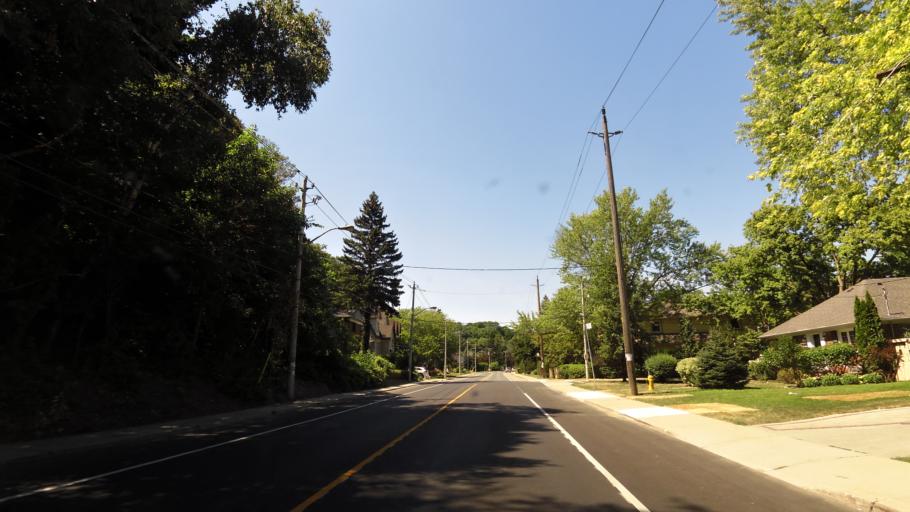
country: CA
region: Ontario
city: Toronto
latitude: 43.6419
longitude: -79.4798
